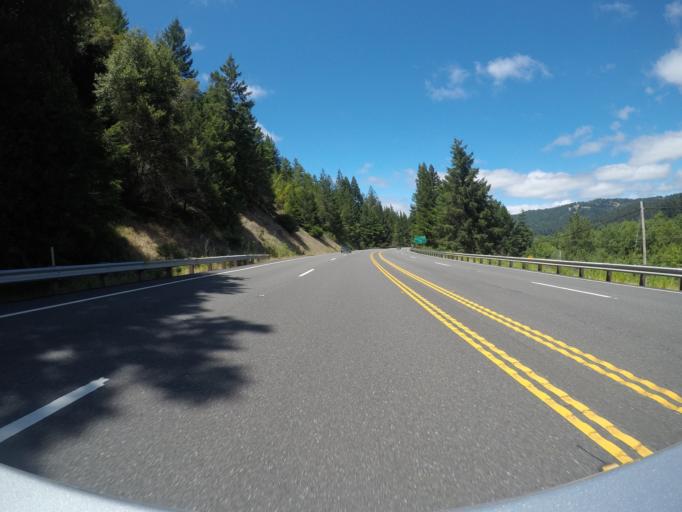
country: US
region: California
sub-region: Humboldt County
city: Redway
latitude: 40.2335
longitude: -123.8329
